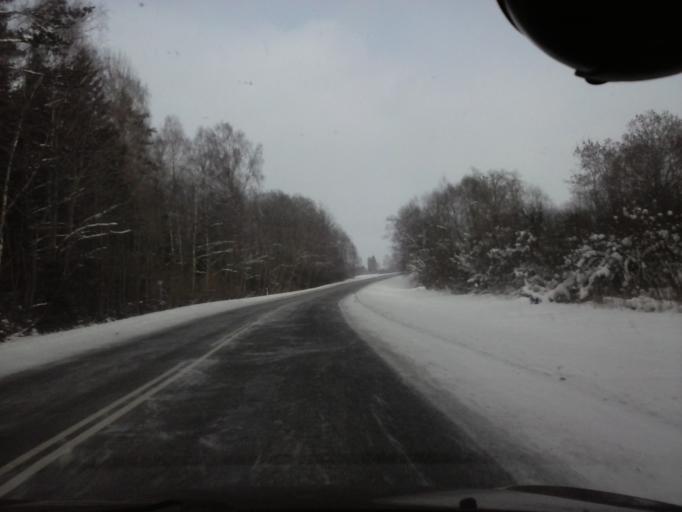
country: EE
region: Viljandimaa
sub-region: Suure-Jaani vald
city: Suure-Jaani
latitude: 58.3499
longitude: 25.3692
